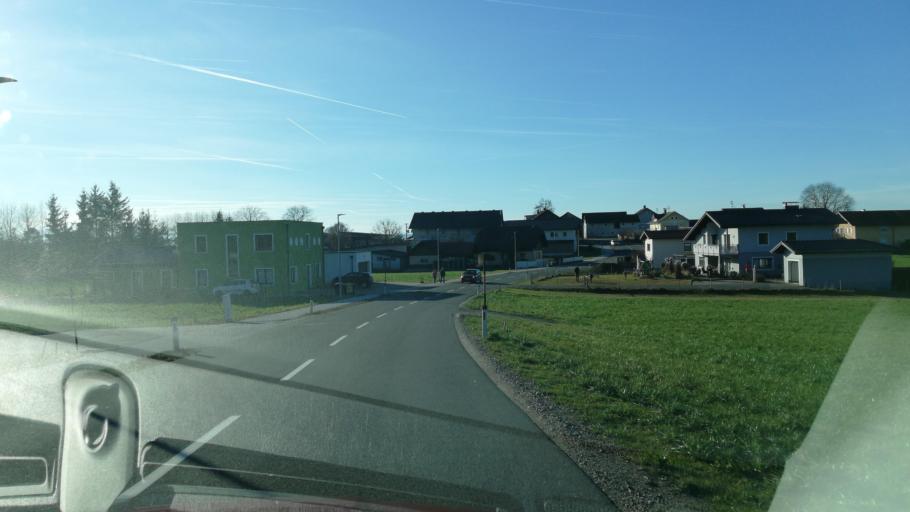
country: DE
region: Bavaria
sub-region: Upper Bavaria
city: Fridolfing
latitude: 48.0503
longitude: 12.8481
